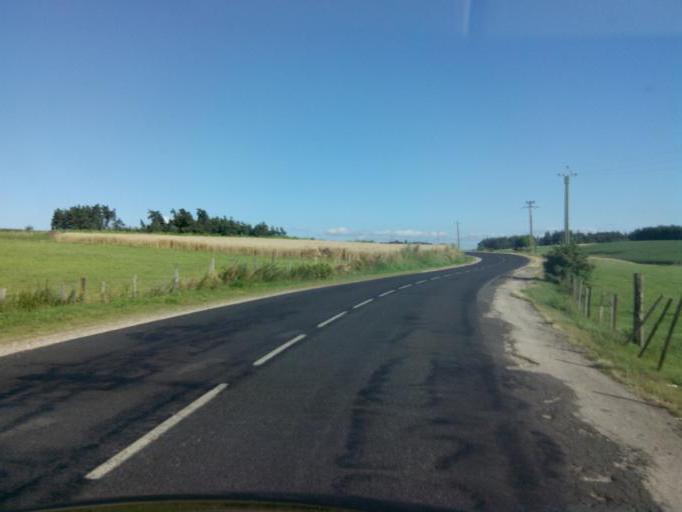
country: FR
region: Rhone-Alpes
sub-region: Departement de la Loire
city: Usson-en-Forez
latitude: 45.3535
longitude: 3.9291
